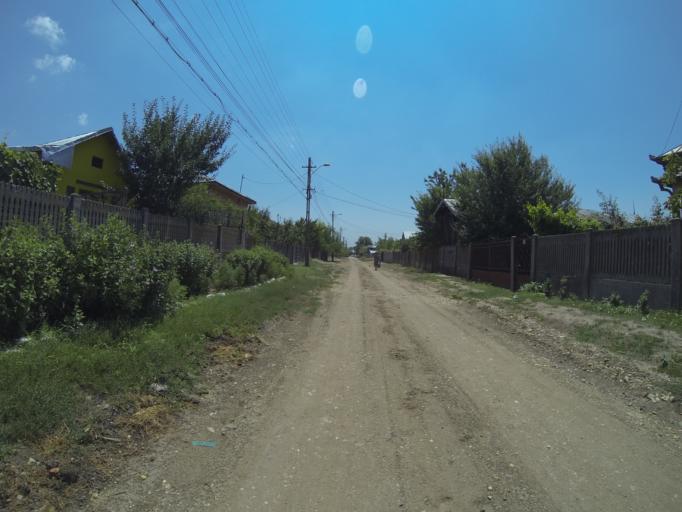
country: RO
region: Dolj
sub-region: Comuna Segarcea
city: Segarcea
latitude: 44.0922
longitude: 23.7475
